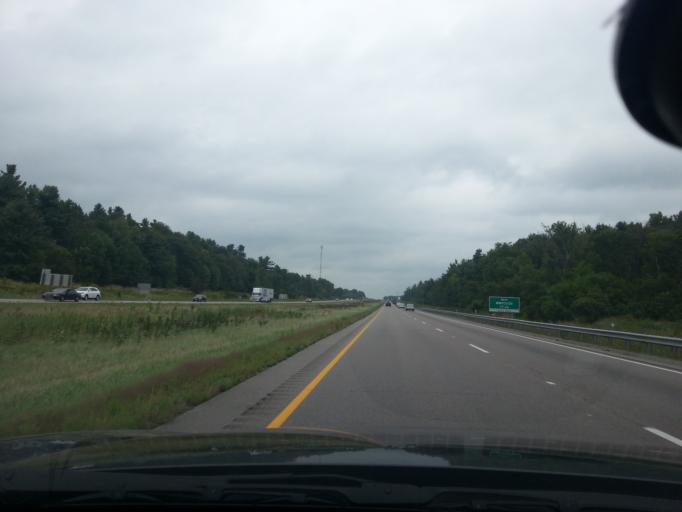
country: US
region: New York
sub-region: Jefferson County
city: Alexandria Bay
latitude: 44.4959
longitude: -75.8477
